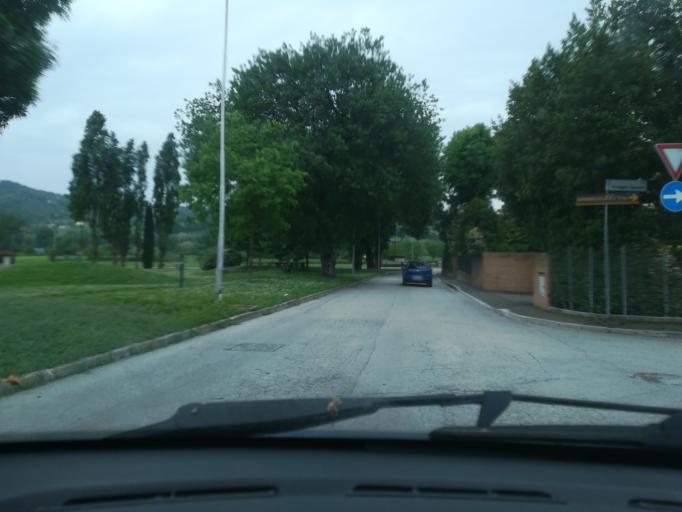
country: IT
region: The Marches
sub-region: Provincia di Macerata
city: Passo di Treia
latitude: 43.2807
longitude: 13.3227
